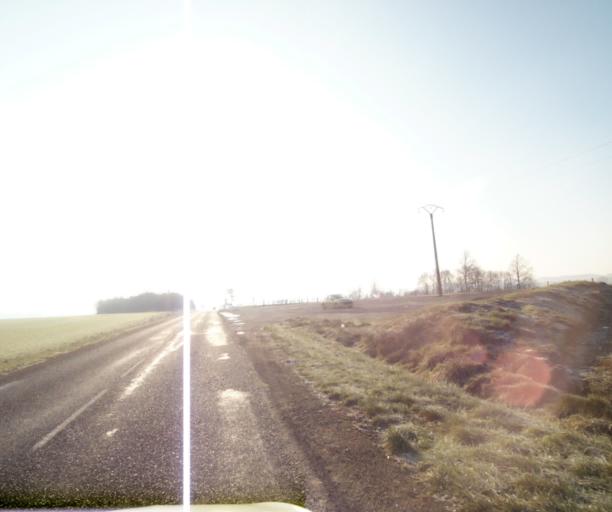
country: FR
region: Champagne-Ardenne
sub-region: Departement de la Haute-Marne
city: Montier-en-Der
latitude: 48.4963
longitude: 4.7536
